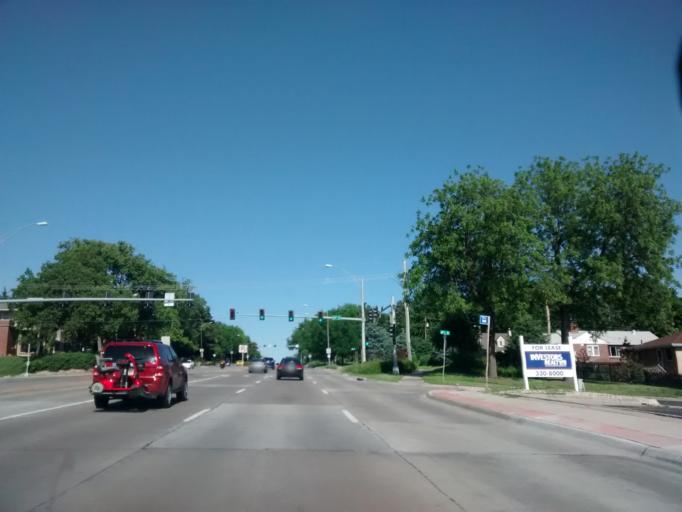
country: US
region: Nebraska
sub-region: Douglas County
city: Ralston
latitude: 41.2596
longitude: -96.0201
